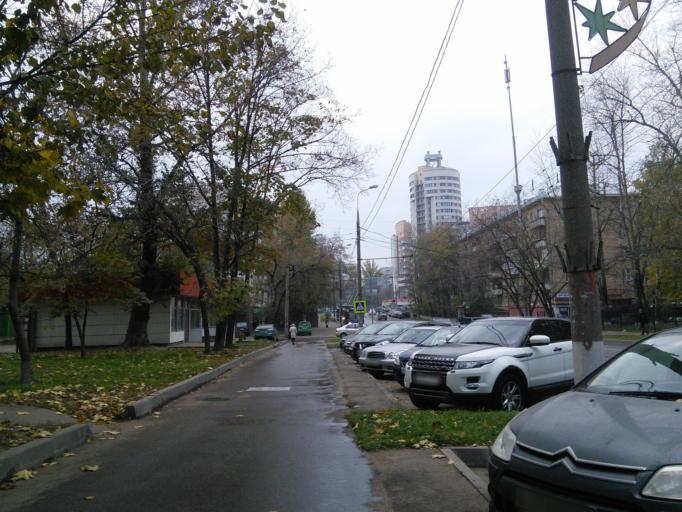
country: RU
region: Moskovskaya
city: Khoroshevo-Mnevniki
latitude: 55.7798
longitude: 37.4613
